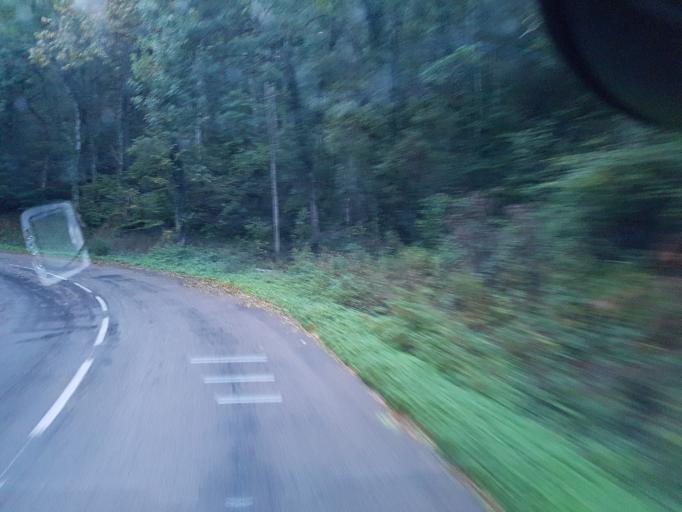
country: FR
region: Midi-Pyrenees
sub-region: Departement du Tarn
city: Mazamet
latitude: 43.4641
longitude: 2.3553
